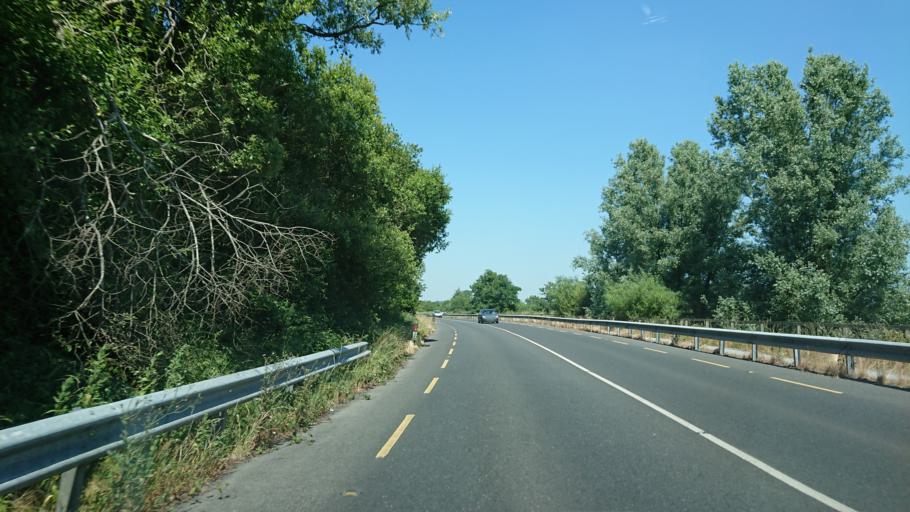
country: IE
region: Munster
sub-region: Waterford
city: Waterford
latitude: 52.2302
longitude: -7.1223
